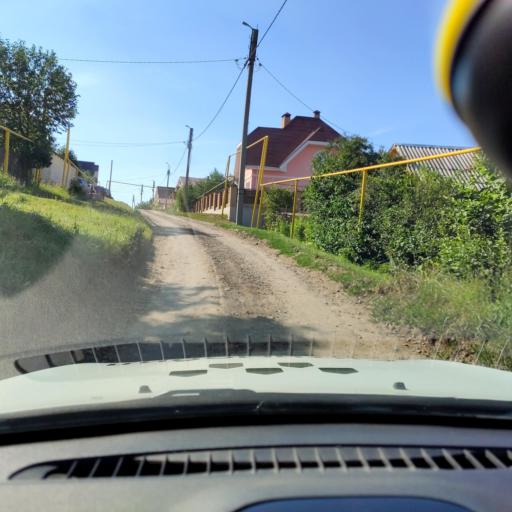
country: RU
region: Samara
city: Zhigulevsk
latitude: 53.3976
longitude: 49.5283
